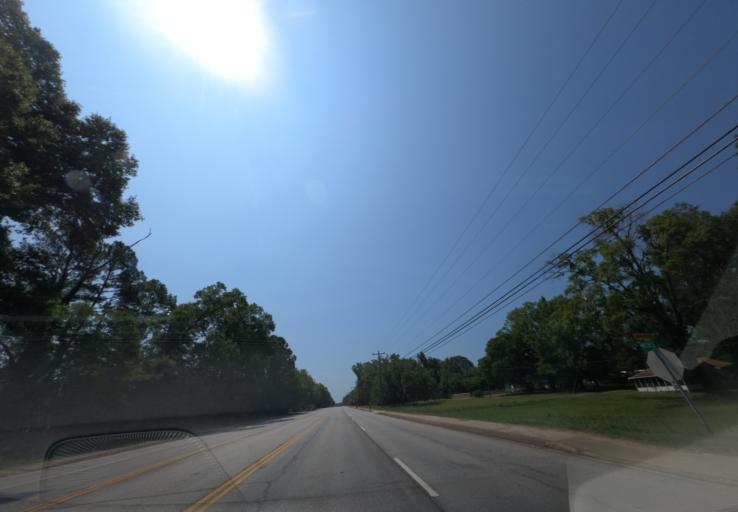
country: US
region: South Carolina
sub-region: Greenwood County
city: Greenwood
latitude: 34.1434
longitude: -82.1336
